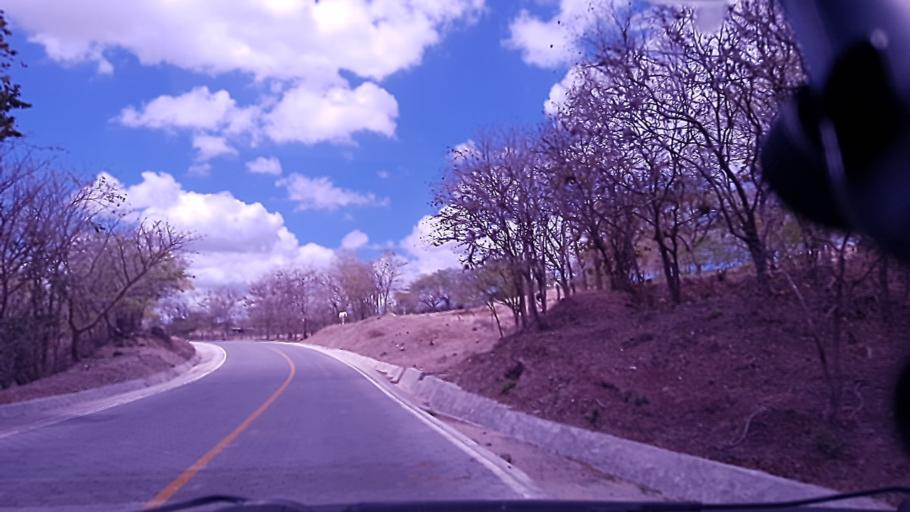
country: NI
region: Esteli
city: Condega
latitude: 13.3730
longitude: -86.3761
